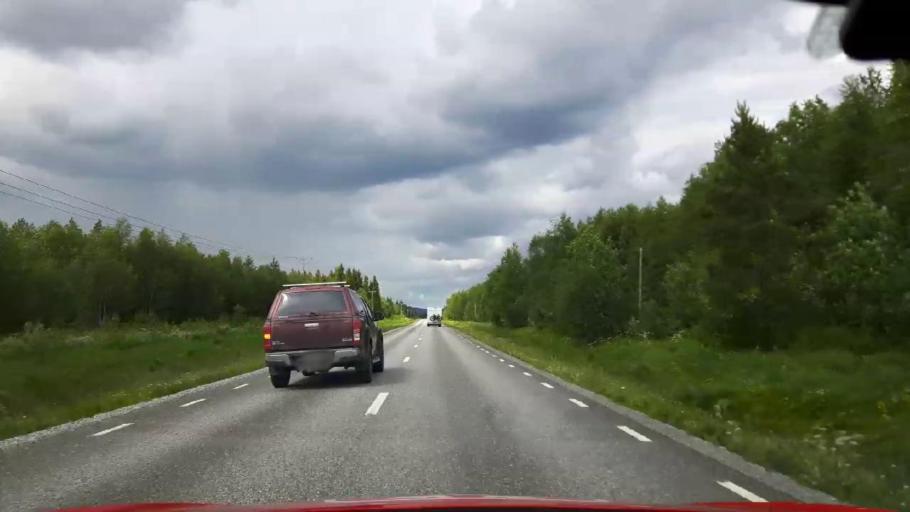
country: SE
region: Jaemtland
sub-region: Krokoms Kommun
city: Krokom
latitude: 63.6602
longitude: 14.3632
